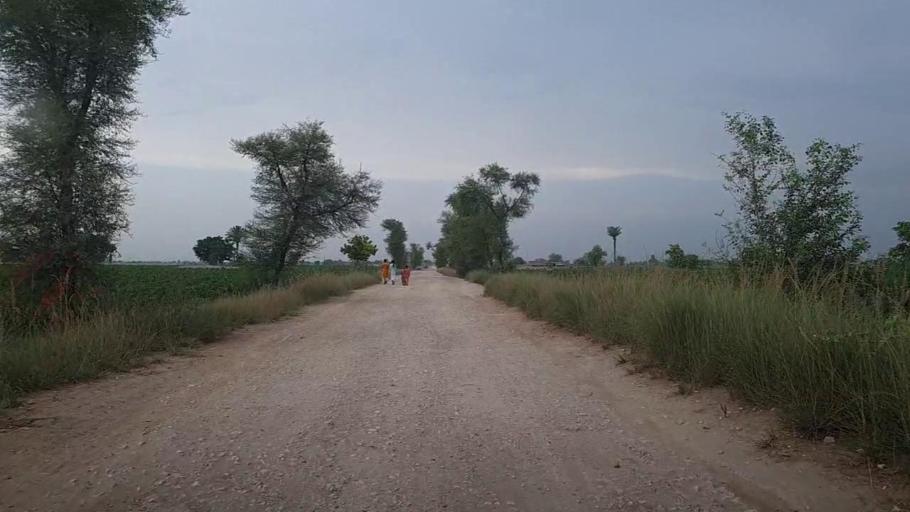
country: PK
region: Sindh
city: Karaundi
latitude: 26.9648
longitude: 68.3438
